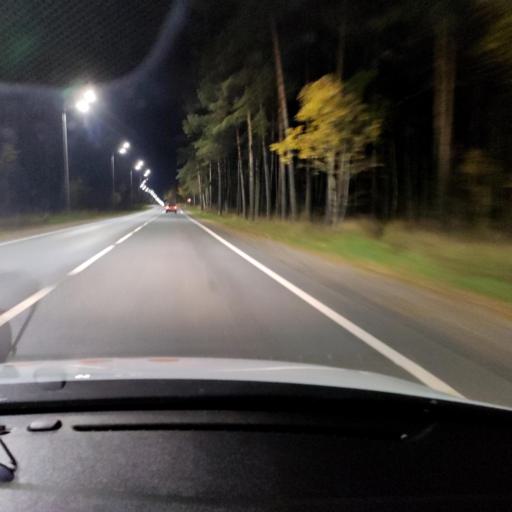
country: RU
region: Tatarstan
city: Stolbishchi
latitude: 55.6346
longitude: 49.0839
